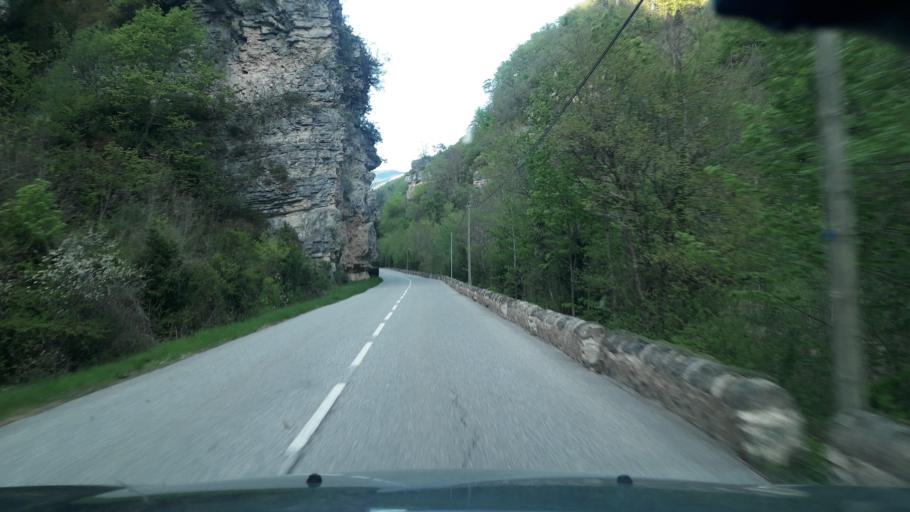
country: FR
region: Rhone-Alpes
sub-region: Departement de la Drome
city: Die
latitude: 44.6686
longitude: 5.5534
